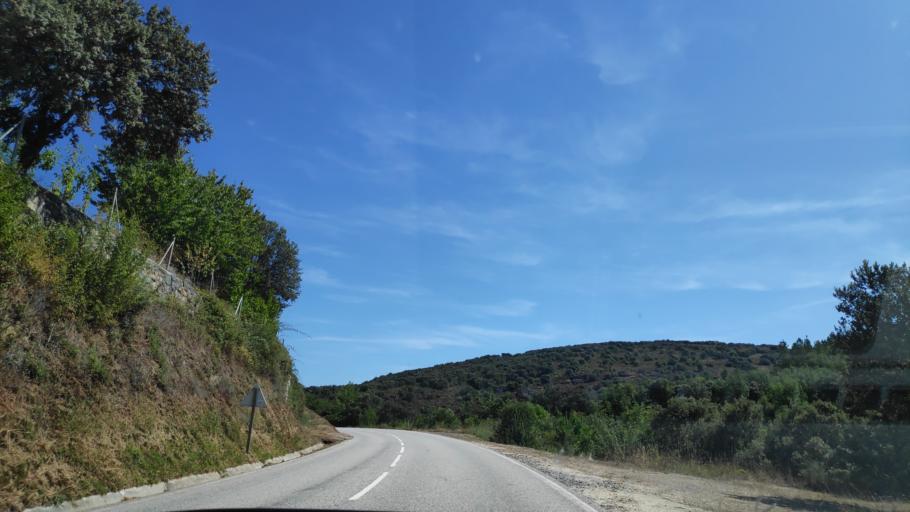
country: PT
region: Braganca
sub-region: Braganca Municipality
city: Braganca
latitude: 41.8307
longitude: -6.7500
